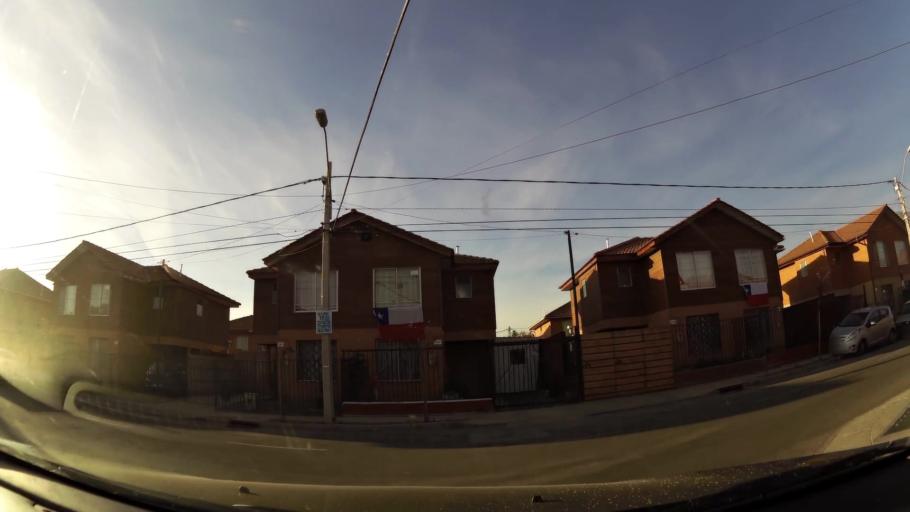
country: CL
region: Santiago Metropolitan
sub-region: Provincia de Cordillera
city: Puente Alto
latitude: -33.5954
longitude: -70.5518
